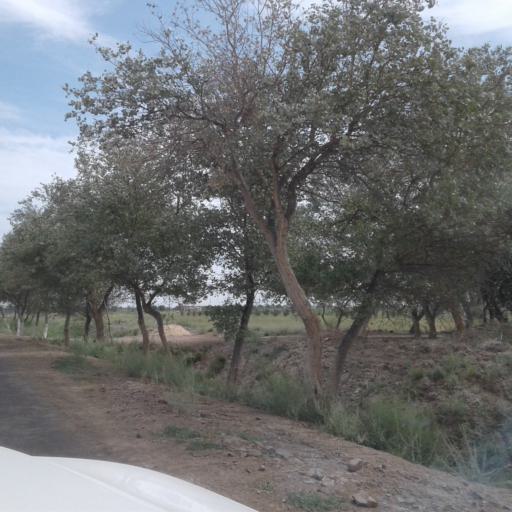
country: TM
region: Dasoguz
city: Tagta
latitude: 41.5673
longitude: 59.8166
